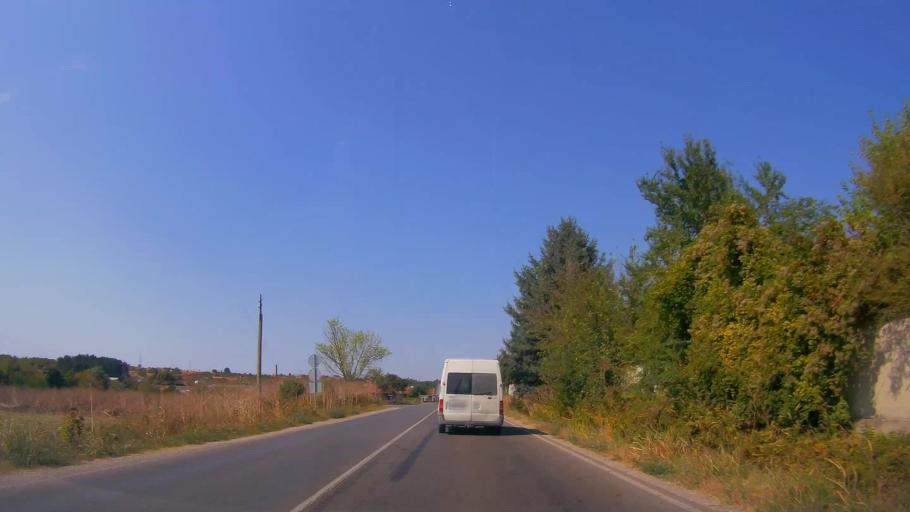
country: BG
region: Razgrad
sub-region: Obshtina Tsar Kaloyan
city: Tsar Kaloyan
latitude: 43.5998
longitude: 26.2467
